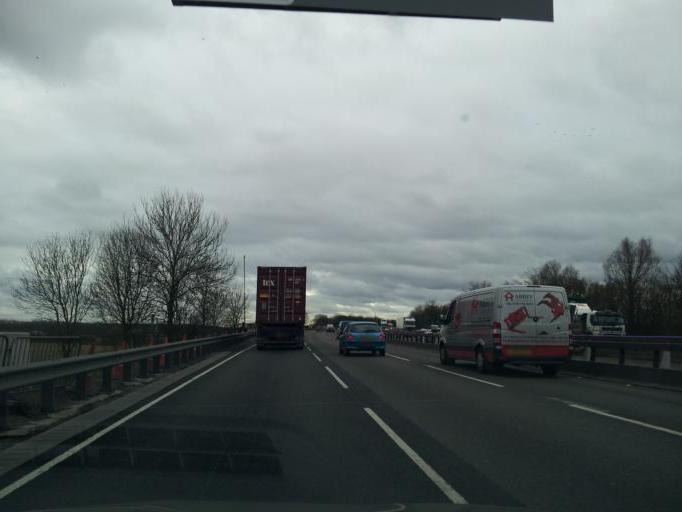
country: GB
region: England
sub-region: Staffordshire
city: Penkridge
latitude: 52.7110
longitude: -2.1006
